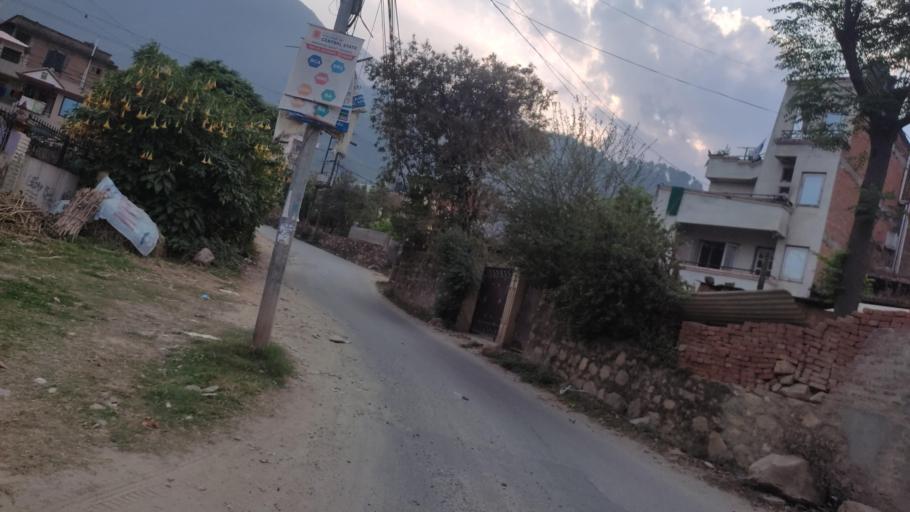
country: NP
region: Central Region
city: Kirtipur
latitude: 27.6660
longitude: 85.2553
